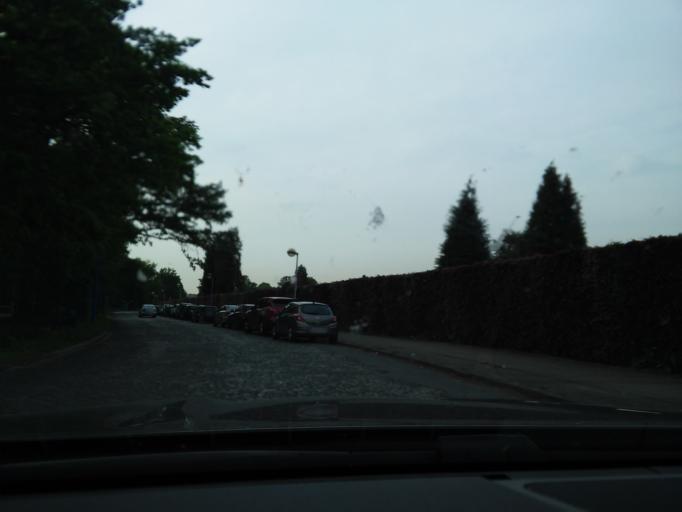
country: BE
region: Flanders
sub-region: Provincie Antwerpen
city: Mortsel
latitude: 51.1838
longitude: 4.4226
